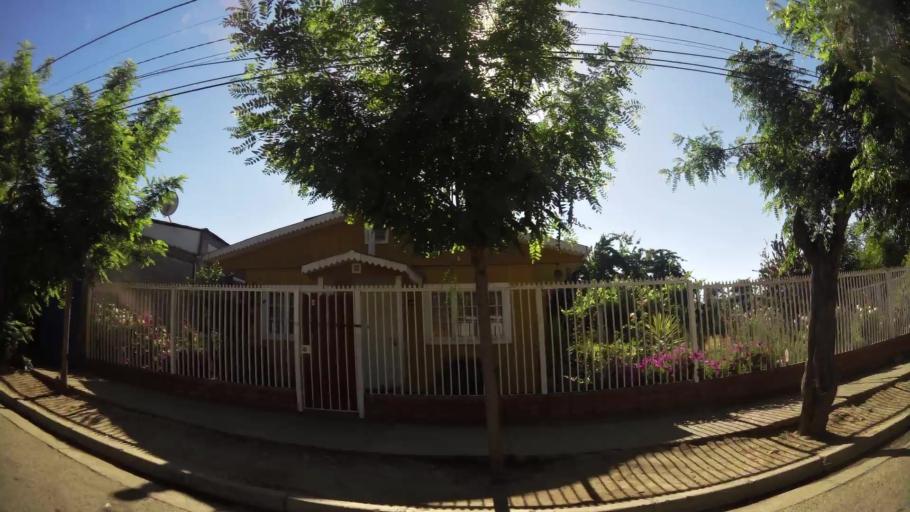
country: CL
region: Santiago Metropolitan
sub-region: Provincia de Chacabuco
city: Lampa
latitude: -33.3980
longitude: -71.1287
